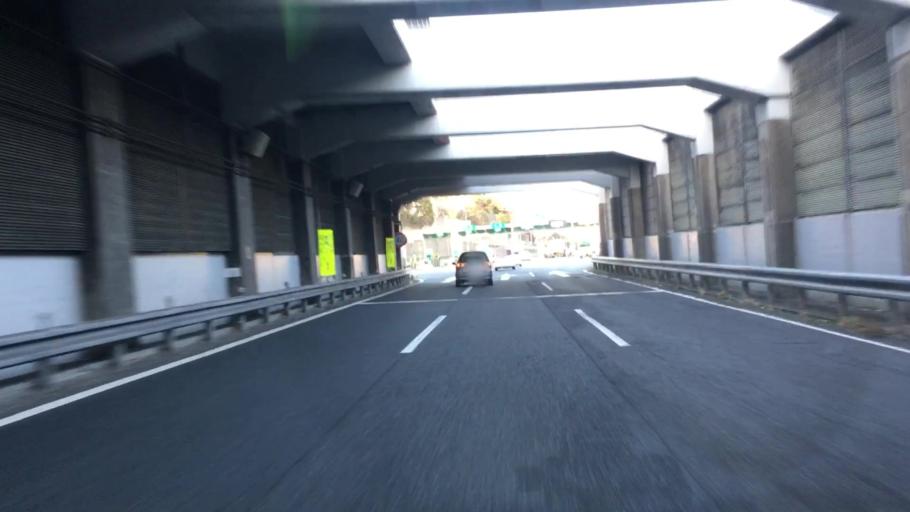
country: JP
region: Kanagawa
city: Yokohama
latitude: 35.4224
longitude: 139.5803
